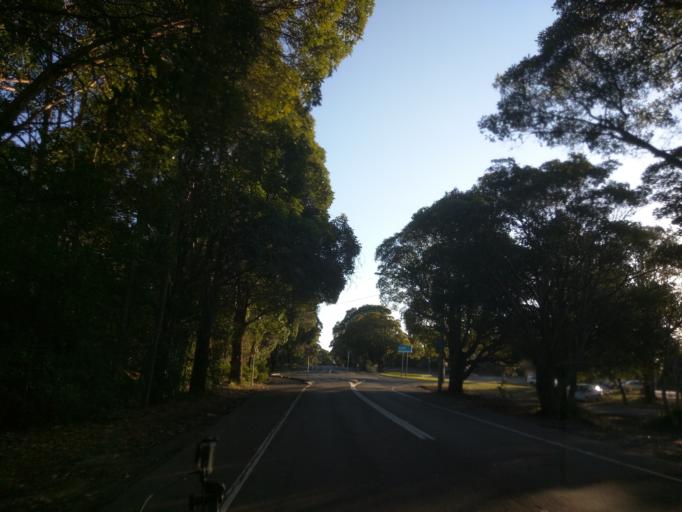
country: AU
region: New South Wales
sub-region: Sutherland Shire
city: Loftus
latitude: -34.0381
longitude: 151.0543
